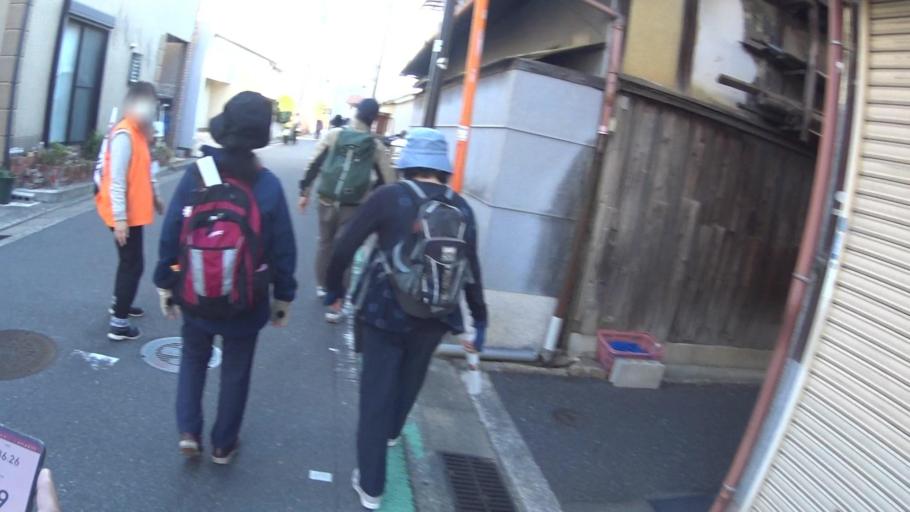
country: JP
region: Osaka
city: Kashihara
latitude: 34.5775
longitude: 135.5939
